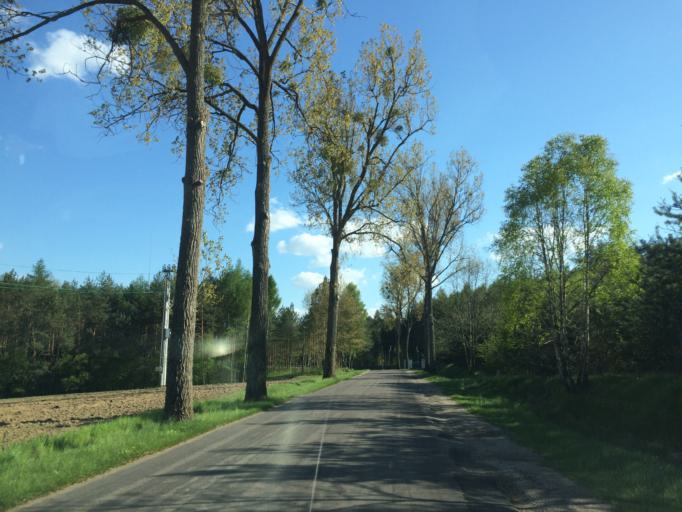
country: PL
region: Warmian-Masurian Voivodeship
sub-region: Powiat dzialdowski
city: Rybno
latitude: 53.3695
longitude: 19.9368
